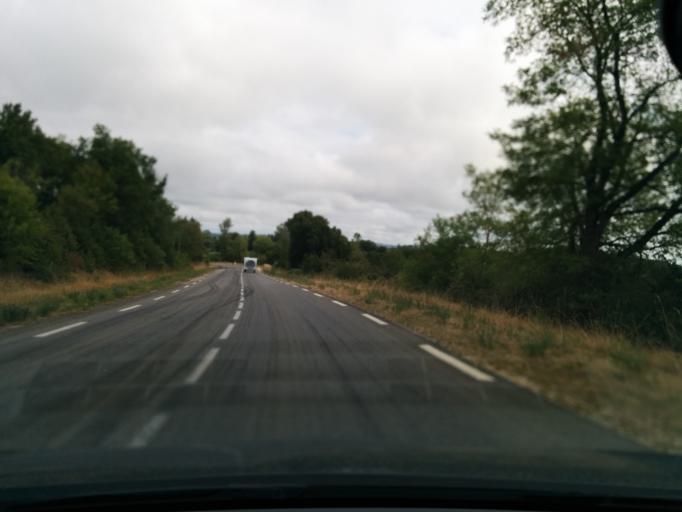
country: FR
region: Midi-Pyrenees
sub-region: Departement du Lot
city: Le Vigan
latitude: 44.6248
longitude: 1.4907
